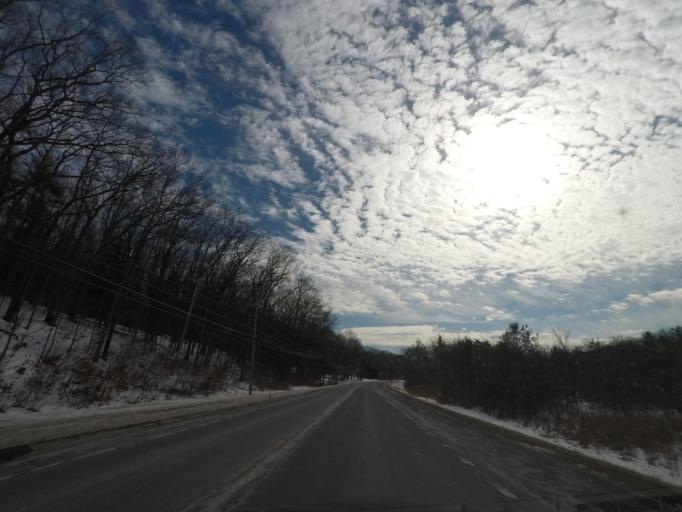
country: US
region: New York
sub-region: Albany County
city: Voorheesville
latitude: 42.6665
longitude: -73.9129
